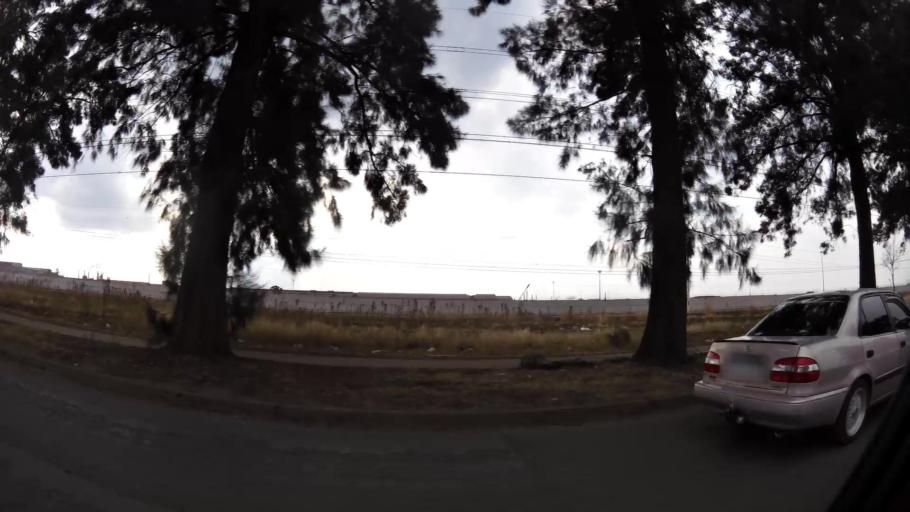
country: ZA
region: Gauteng
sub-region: Sedibeng District Municipality
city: Vanderbijlpark
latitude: -26.6740
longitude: 27.8271
